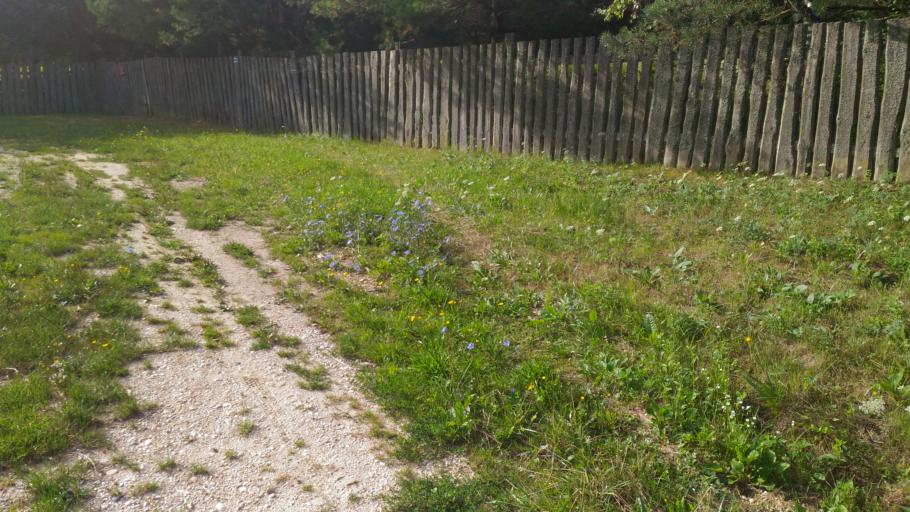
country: HU
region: Zala
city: Zalalovo
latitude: 46.7907
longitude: 16.5275
